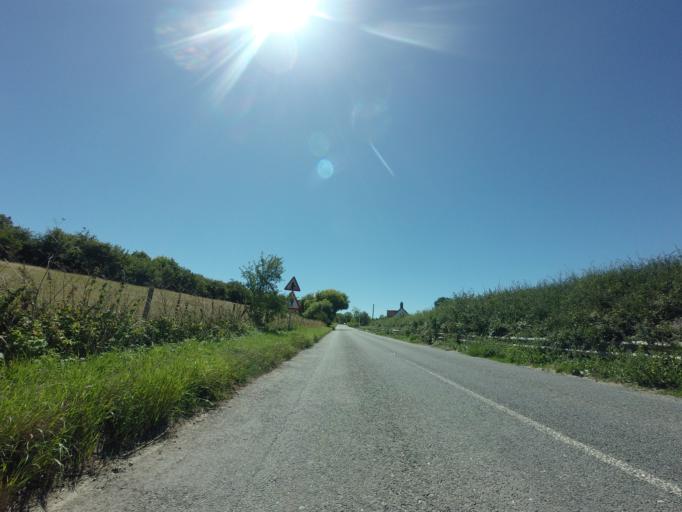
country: GB
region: England
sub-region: Kent
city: Eastry
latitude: 51.2126
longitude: 1.2997
